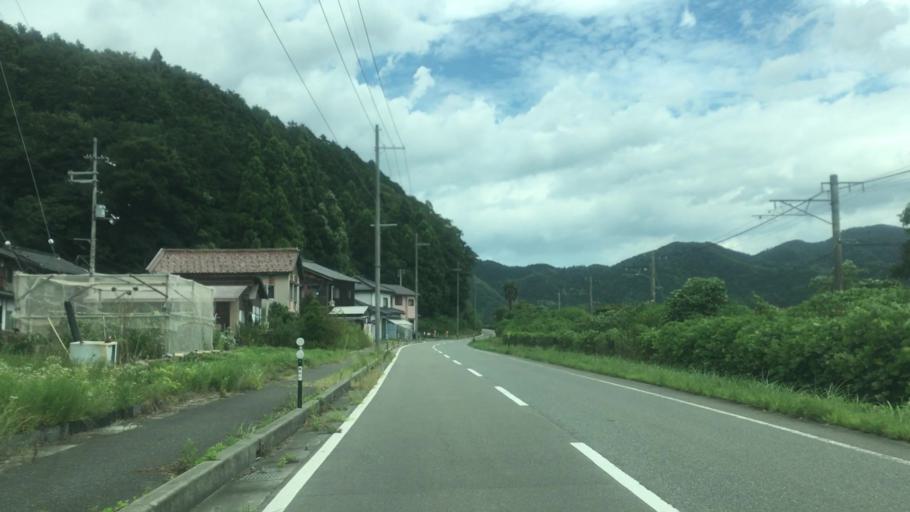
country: JP
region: Hyogo
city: Toyooka
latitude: 35.5704
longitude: 134.8043
